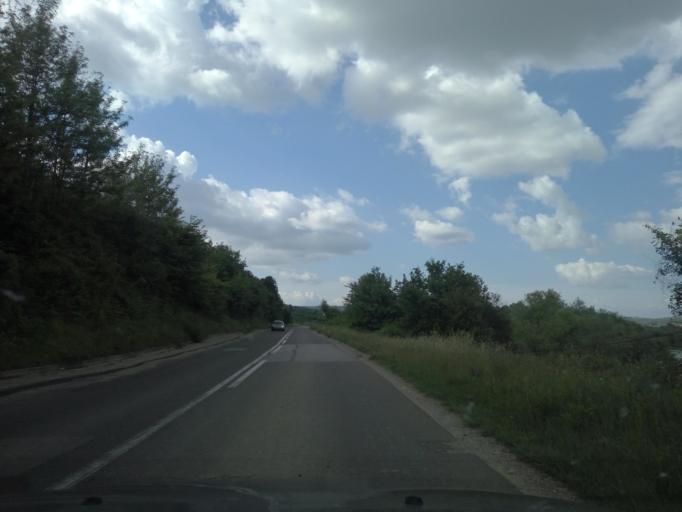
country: XK
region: Pec
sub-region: Komuna e Pejes
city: Kosuriq
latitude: 42.4654
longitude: 20.5050
